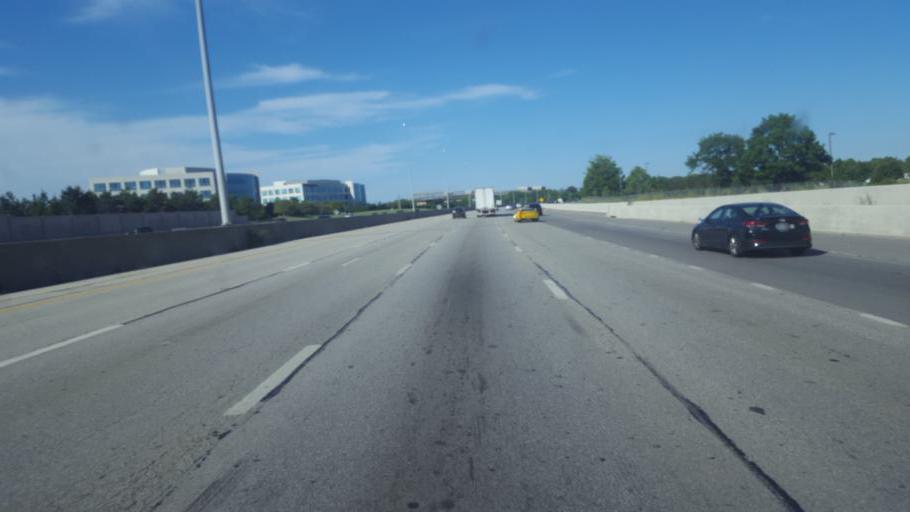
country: US
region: Ohio
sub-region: Franklin County
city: Dublin
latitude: 40.1028
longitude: -83.1304
